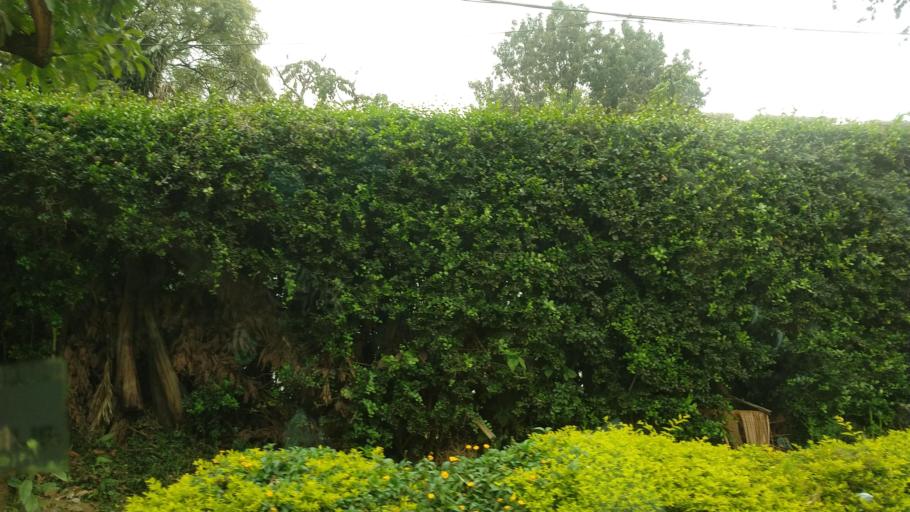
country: KE
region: Nairobi Area
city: Nairobi
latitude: -1.2916
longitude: 36.7816
